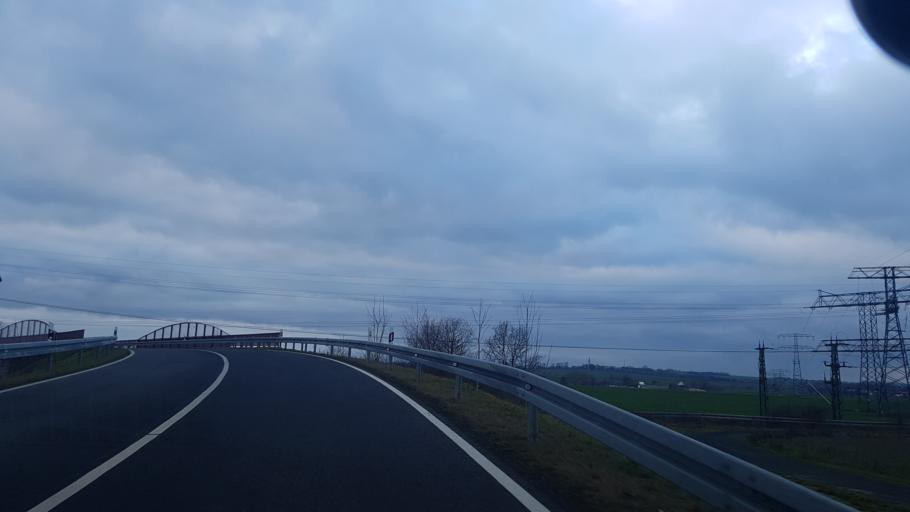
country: DE
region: Saxony
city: Priestewitz
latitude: 51.2388
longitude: 13.5451
